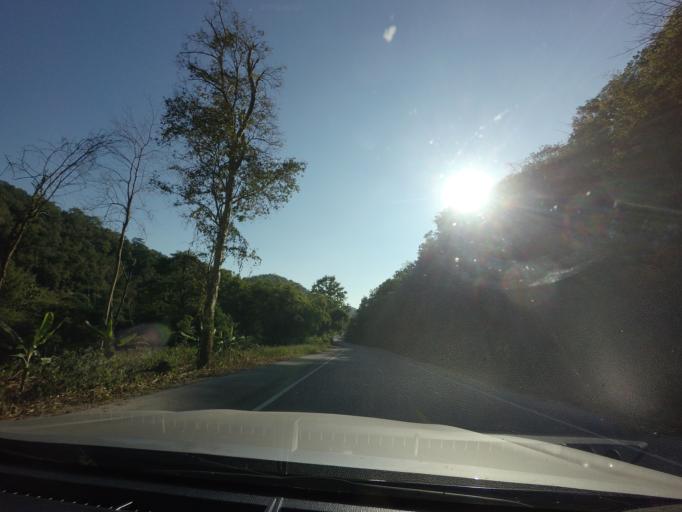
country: TH
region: Lampang
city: Chae Hom
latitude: 18.5577
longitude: 99.6273
